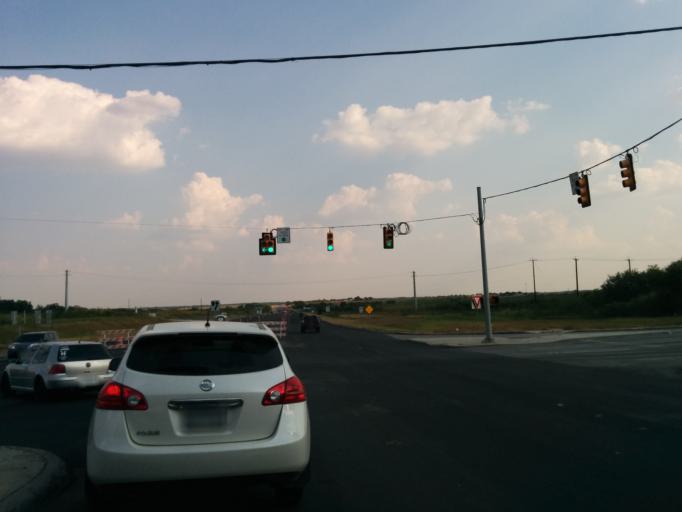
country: US
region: Texas
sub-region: Bexar County
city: Converse
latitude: 29.4651
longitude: -98.2922
